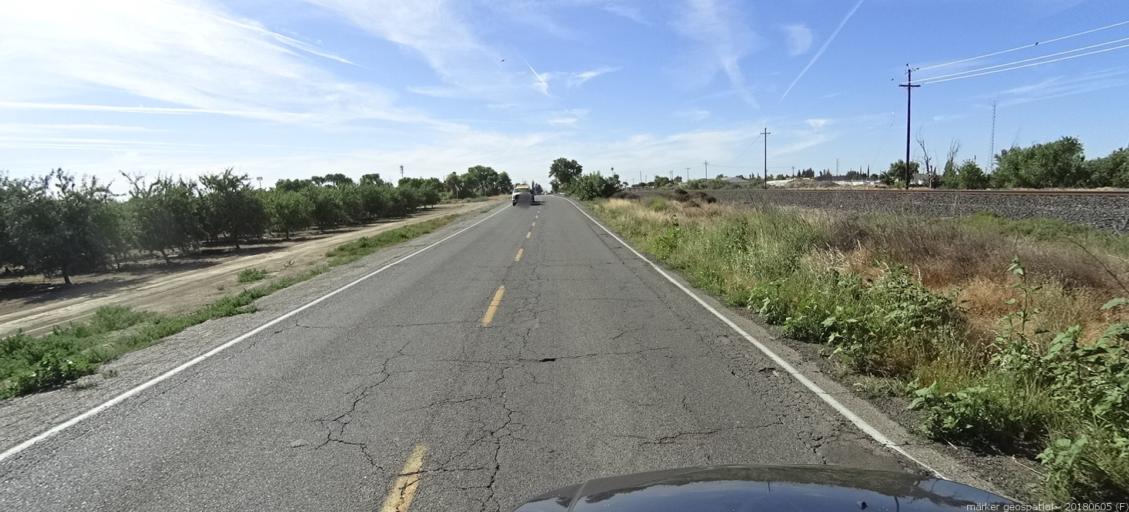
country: US
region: California
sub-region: Madera County
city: Chowchilla
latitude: 37.1284
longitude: -120.2613
